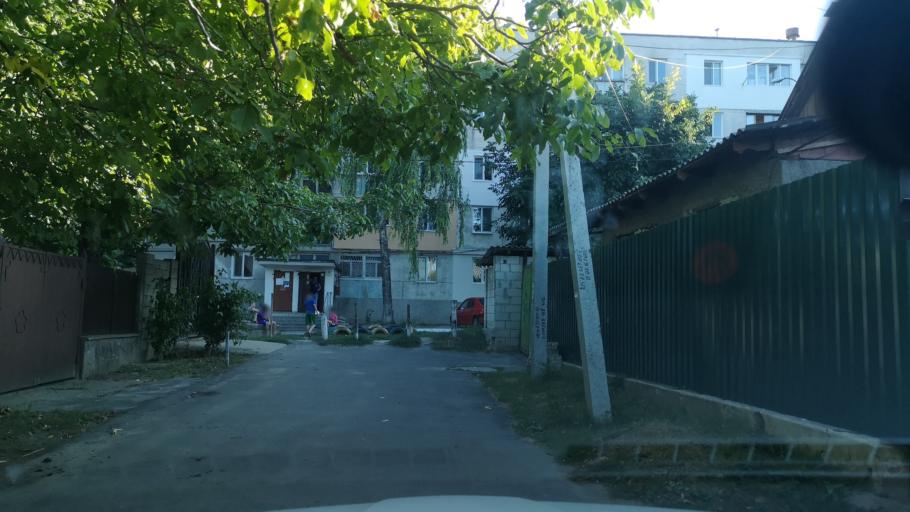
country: MD
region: Chisinau
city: Chisinau
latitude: 46.9870
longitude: 28.8801
